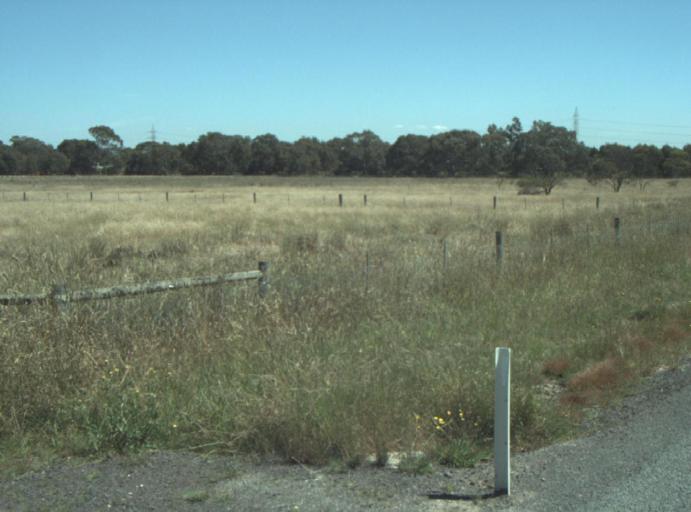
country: AU
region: Victoria
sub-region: Greater Geelong
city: Breakwater
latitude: -38.2053
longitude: 144.3612
